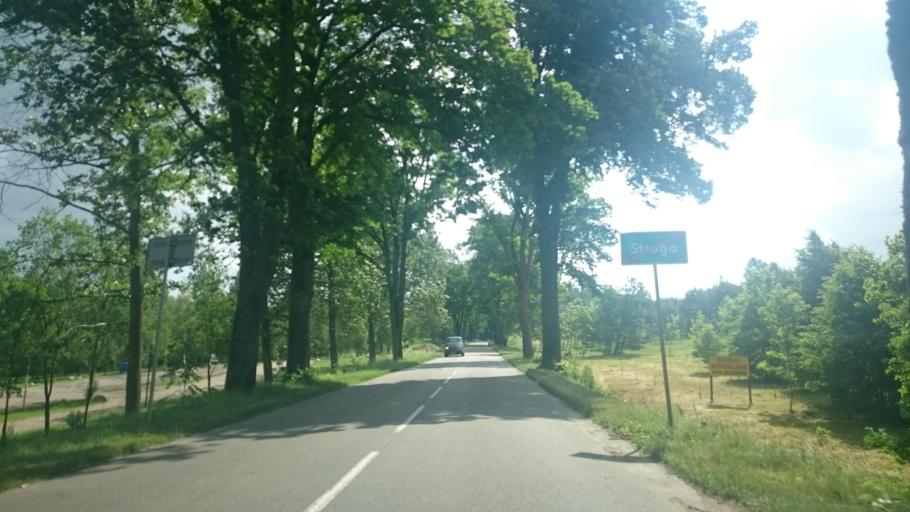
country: PL
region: Pomeranian Voivodeship
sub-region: Powiat starogardzki
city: Zblewo
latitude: 53.9685
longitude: 18.2683
